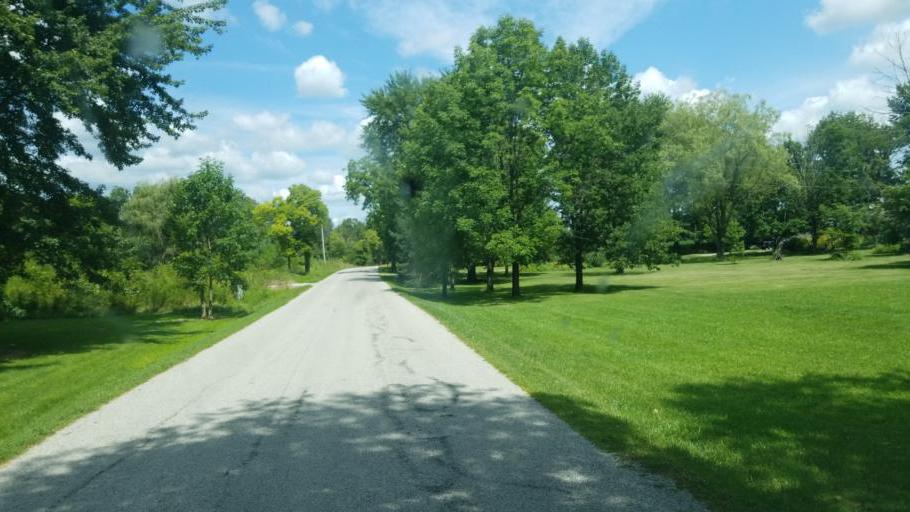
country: US
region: Ohio
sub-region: Delaware County
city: Sunbury
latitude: 40.2849
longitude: -82.8300
